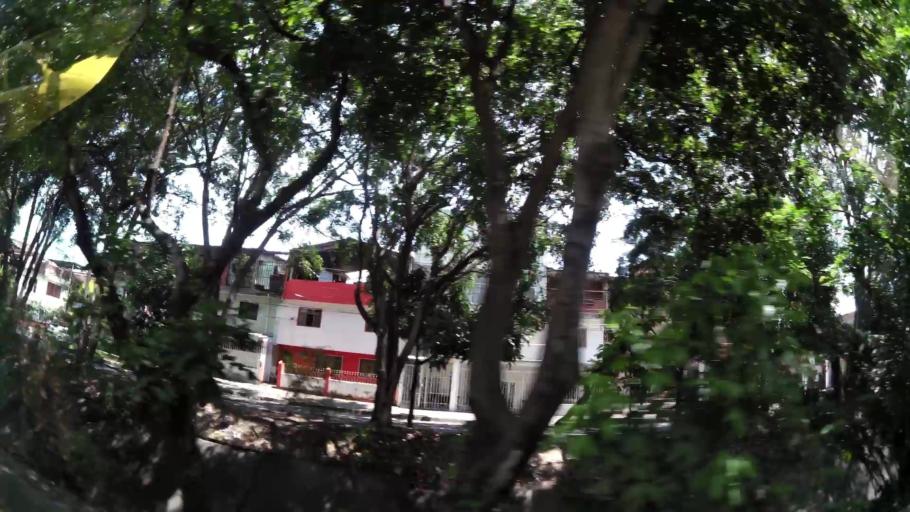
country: CO
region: Valle del Cauca
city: Cali
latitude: 3.4409
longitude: -76.5058
